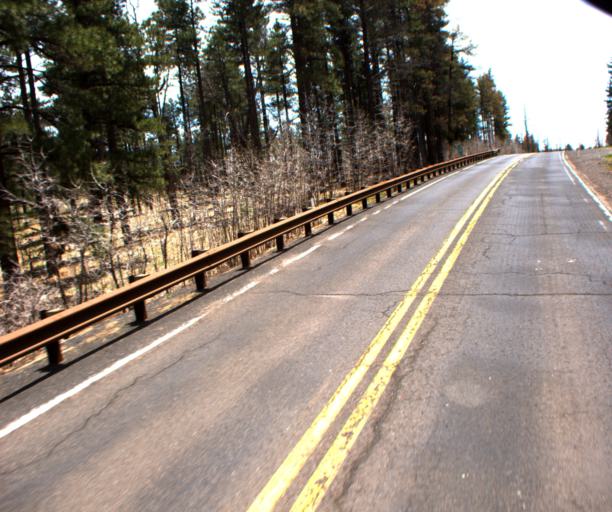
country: US
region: Arizona
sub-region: Coconino County
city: Kachina Village
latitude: 35.0594
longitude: -111.7323
